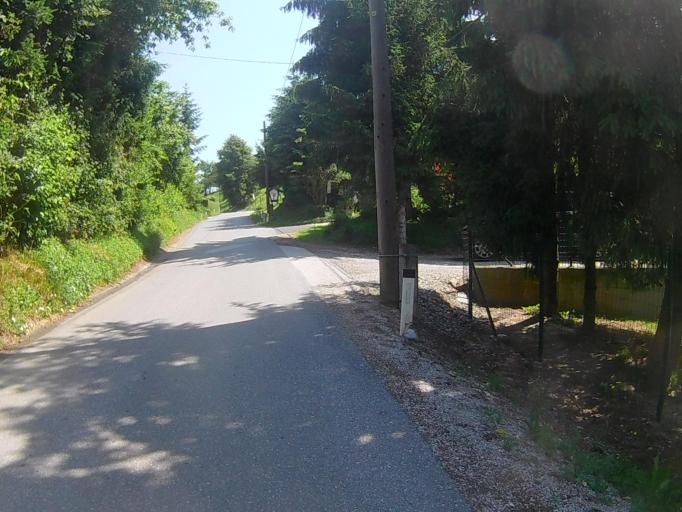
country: SI
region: Pesnica
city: Pesnica pri Mariboru
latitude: 46.5693
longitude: 15.6916
